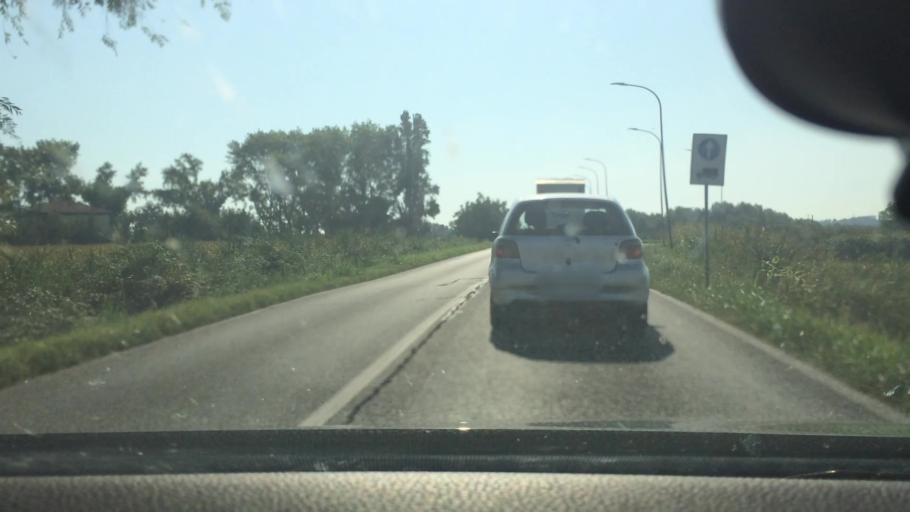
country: IT
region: Emilia-Romagna
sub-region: Provincia di Ferrara
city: Comacchio
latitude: 44.6906
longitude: 12.2027
